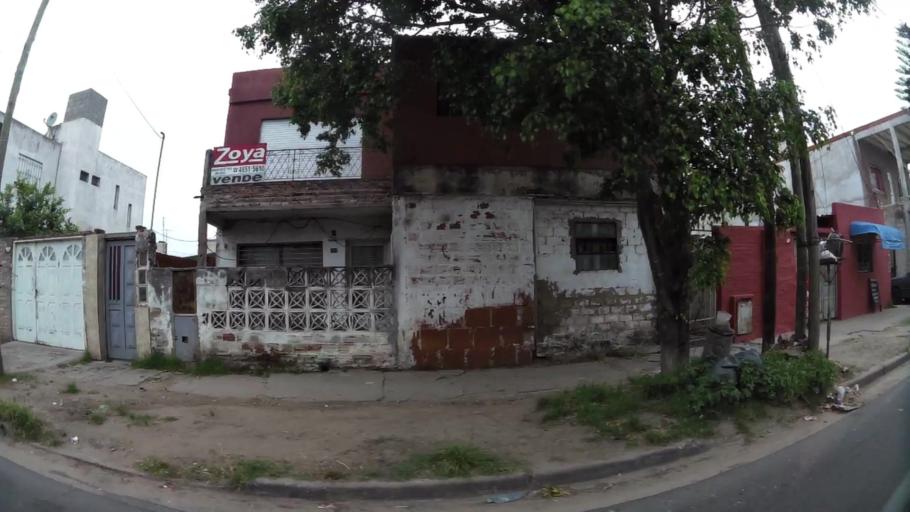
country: AR
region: Buenos Aires
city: San Justo
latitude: -34.6993
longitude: -58.5642
